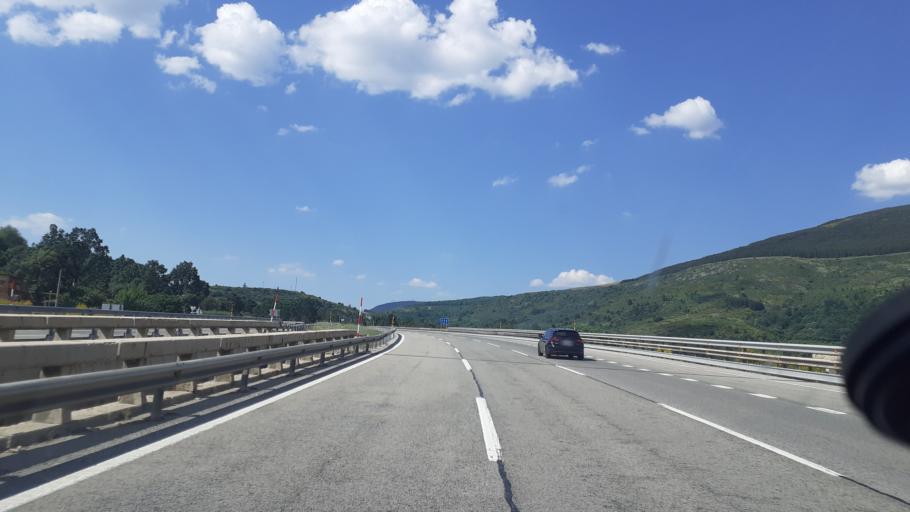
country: ES
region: Madrid
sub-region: Provincia de Madrid
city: Robregordo
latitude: 41.0976
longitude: -3.5925
